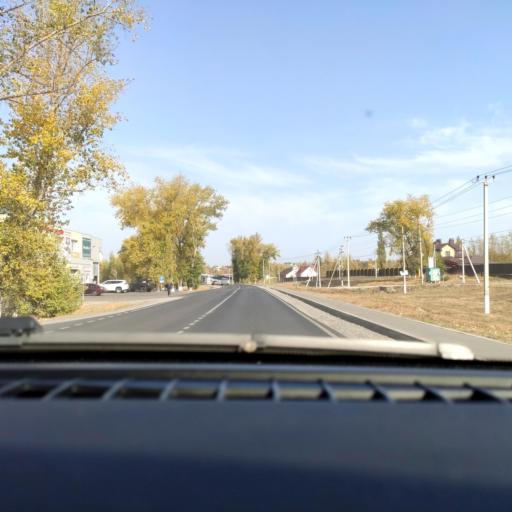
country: RU
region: Voronezj
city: Novaya Usman'
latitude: 51.6662
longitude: 39.4044
